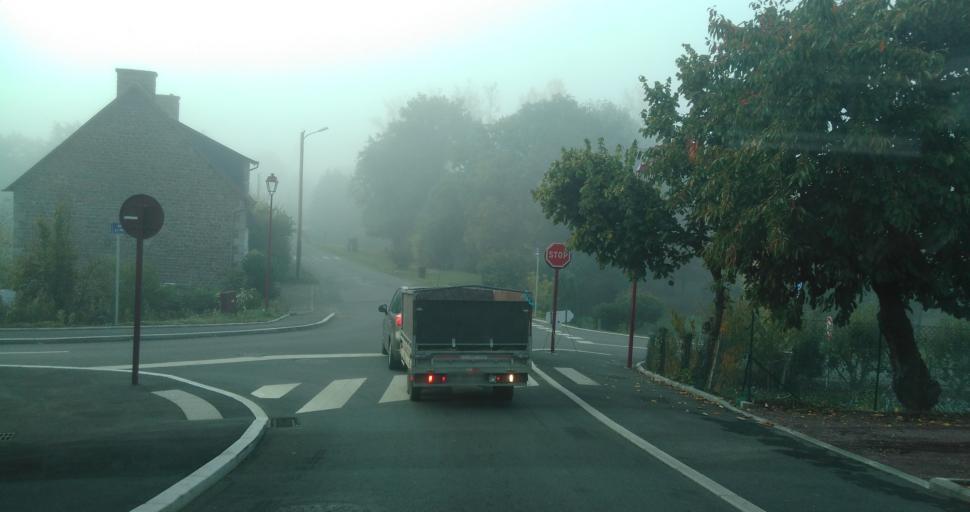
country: FR
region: Brittany
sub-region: Departement d'Ille-et-Vilaine
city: Iffendic
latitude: 48.1278
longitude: -2.0365
